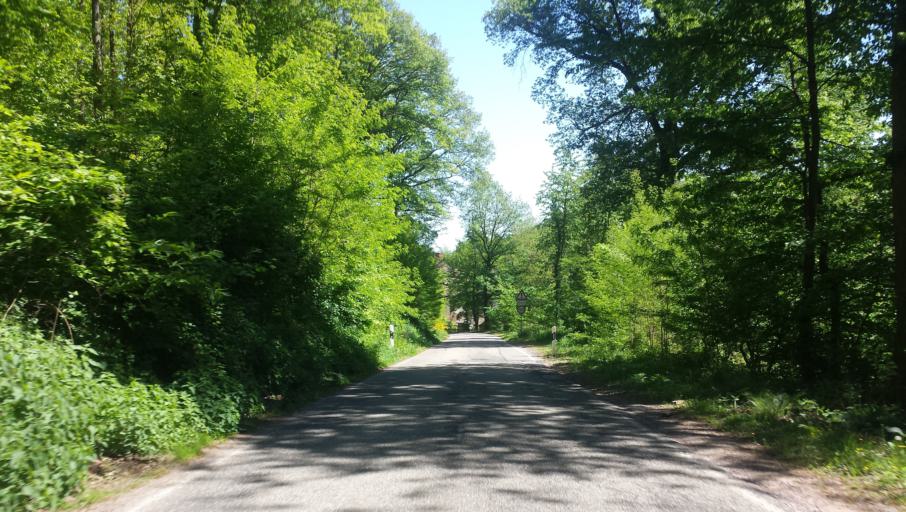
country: DE
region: Rheinland-Pfalz
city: Sankt Martin
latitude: 49.2836
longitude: 8.0855
